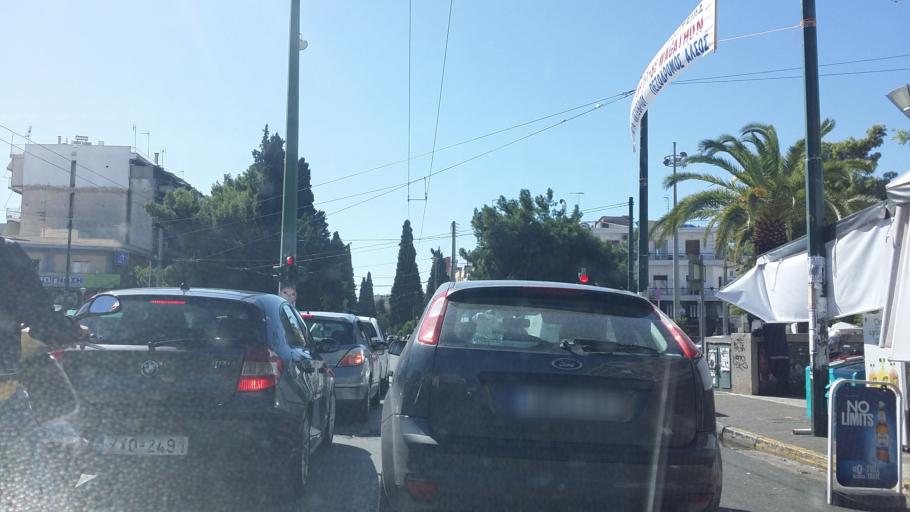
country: GR
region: Attica
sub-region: Nomarchia Athinas
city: Nea Filadelfeia
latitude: 38.0342
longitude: 23.7379
